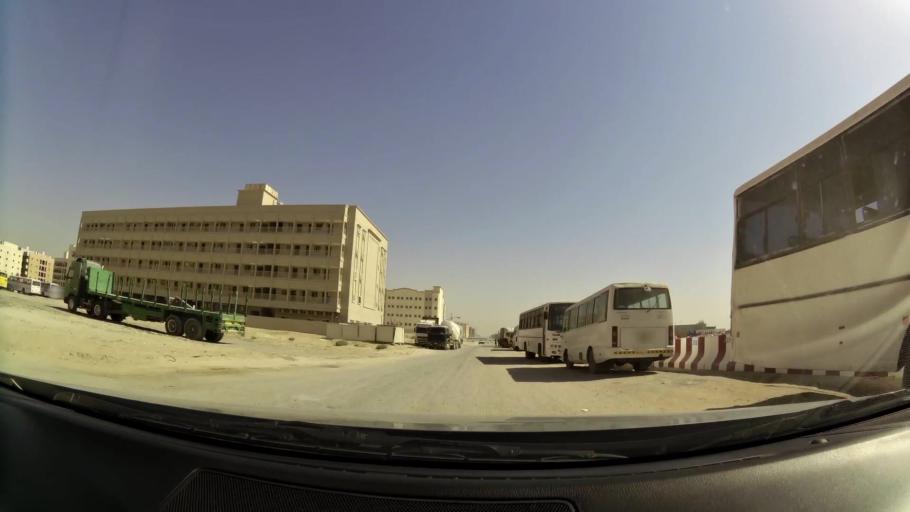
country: AE
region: Dubai
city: Dubai
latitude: 24.9995
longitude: 55.1411
